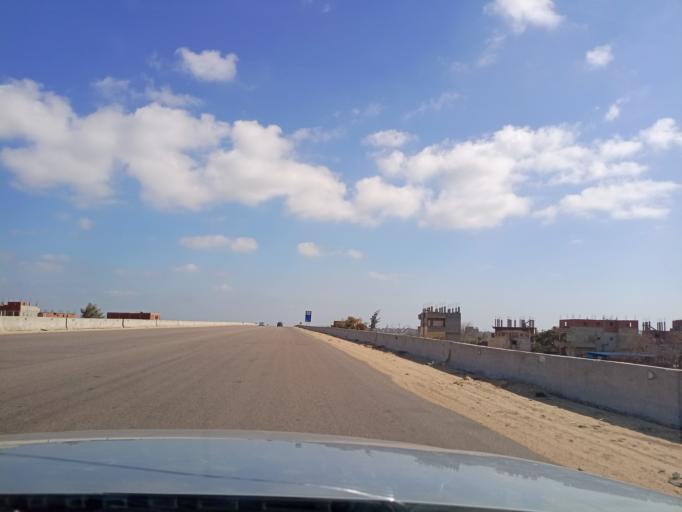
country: EG
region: Muhafazat al Minufiyah
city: Al Bajur
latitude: 30.3964
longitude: 31.0116
